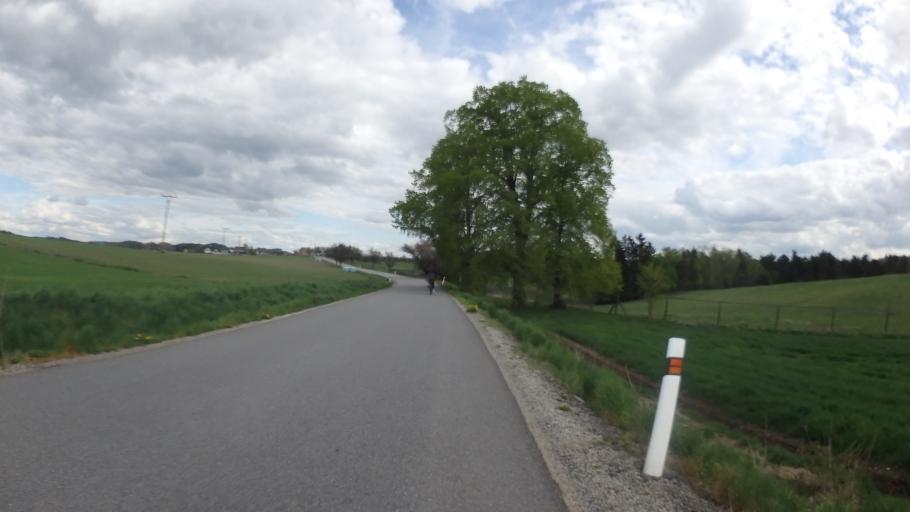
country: CZ
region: Vysocina
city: Merin
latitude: 49.3529
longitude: 15.9260
